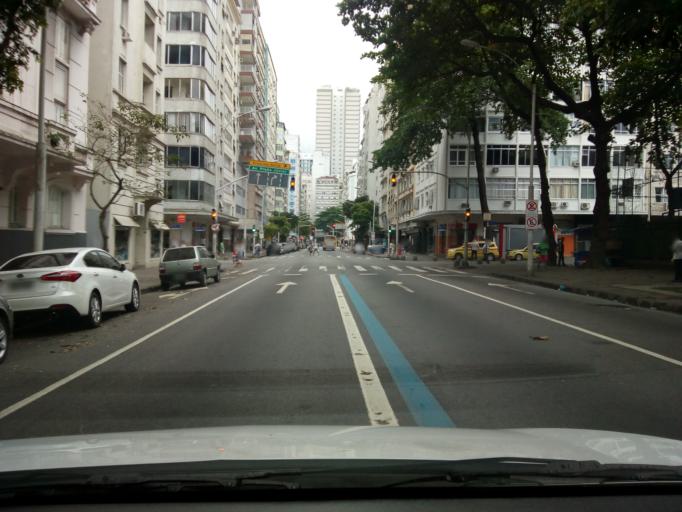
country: BR
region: Rio de Janeiro
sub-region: Rio De Janeiro
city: Rio de Janeiro
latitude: -22.9649
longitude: -43.1763
